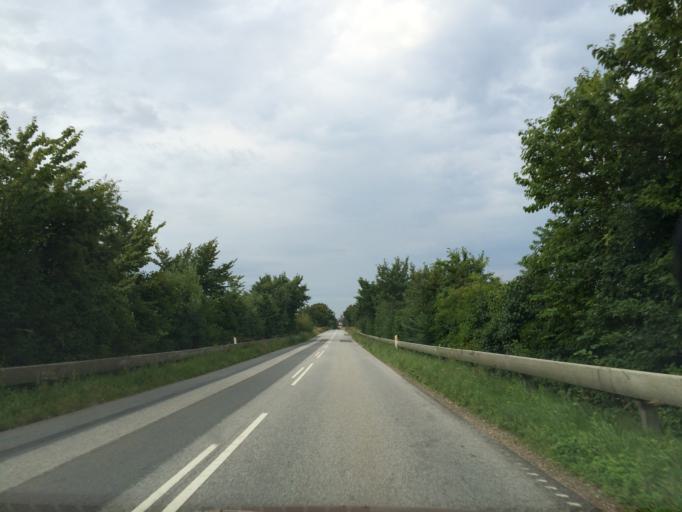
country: DK
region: South Denmark
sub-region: Sonderborg Kommune
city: Broager
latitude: 54.9034
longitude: 9.6752
